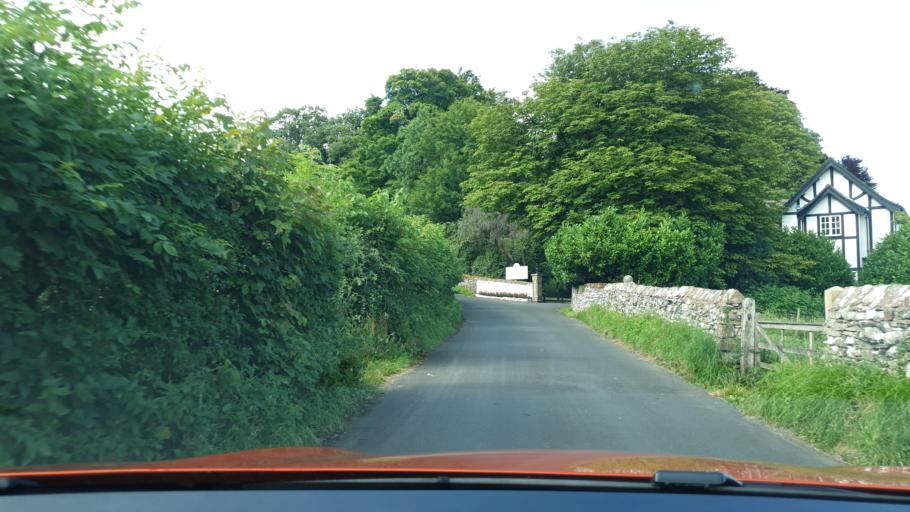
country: GB
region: England
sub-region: Cumbria
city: Penrith
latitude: 54.5923
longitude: -2.8410
